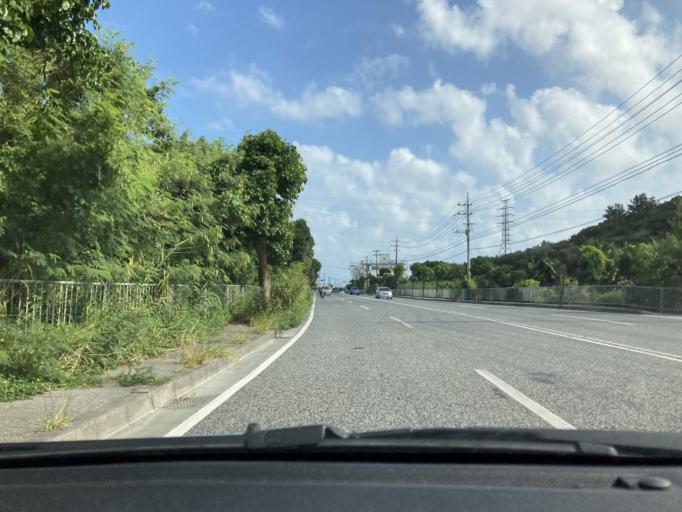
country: JP
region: Okinawa
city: Chatan
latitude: 26.2917
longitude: 127.8109
